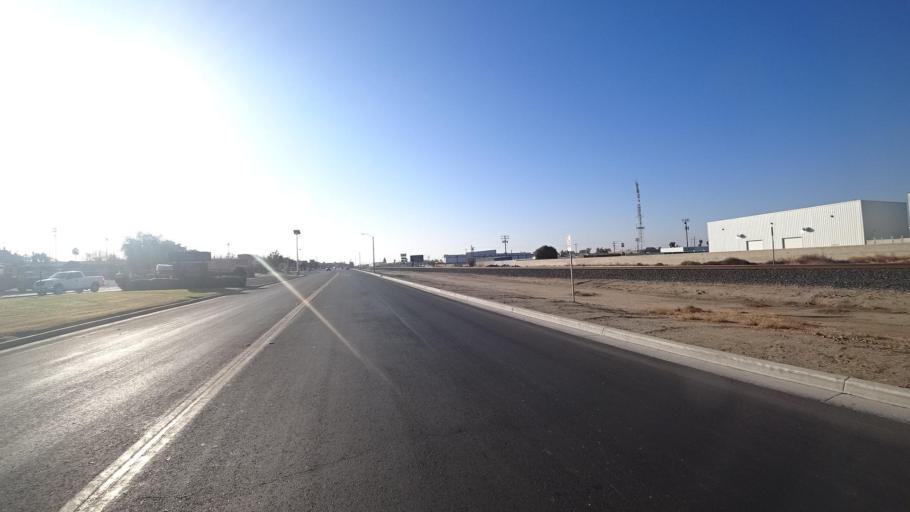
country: US
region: California
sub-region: Kern County
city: Delano
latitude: 35.7794
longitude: -119.2501
